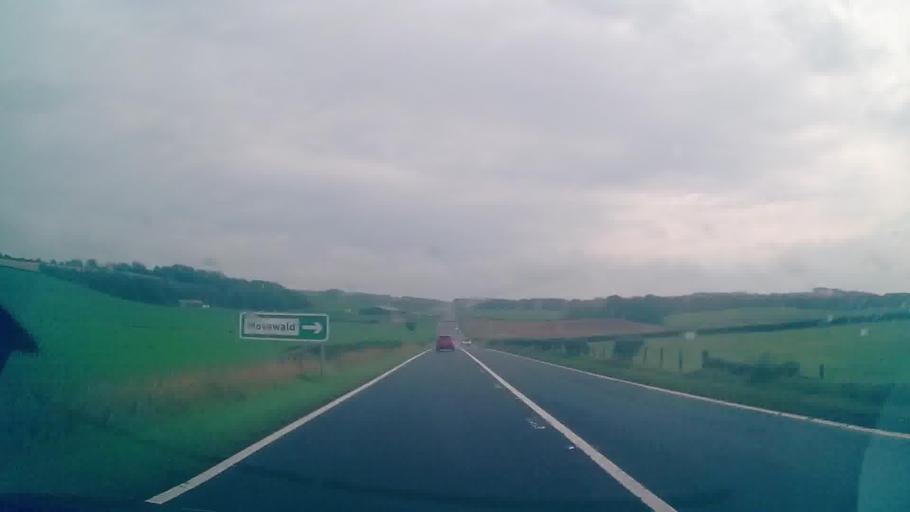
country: GB
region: Scotland
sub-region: Dumfries and Galloway
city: Lochmaben
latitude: 55.0457
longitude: -3.4524
